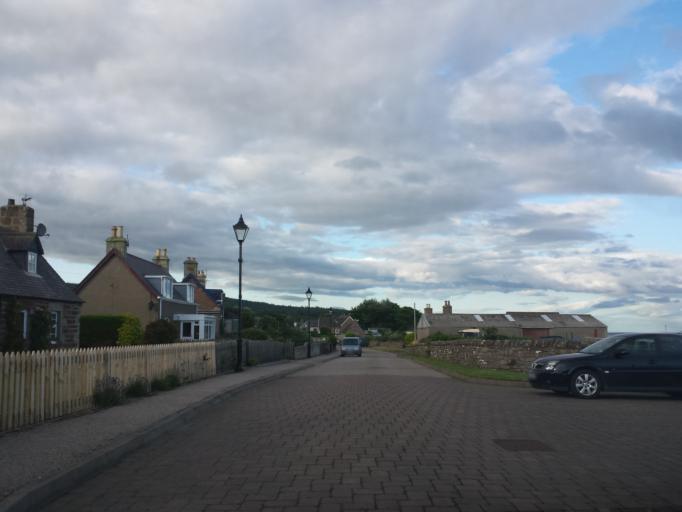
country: GB
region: Scotland
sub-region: Highland
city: Golspie
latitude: 57.9699
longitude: -3.9834
